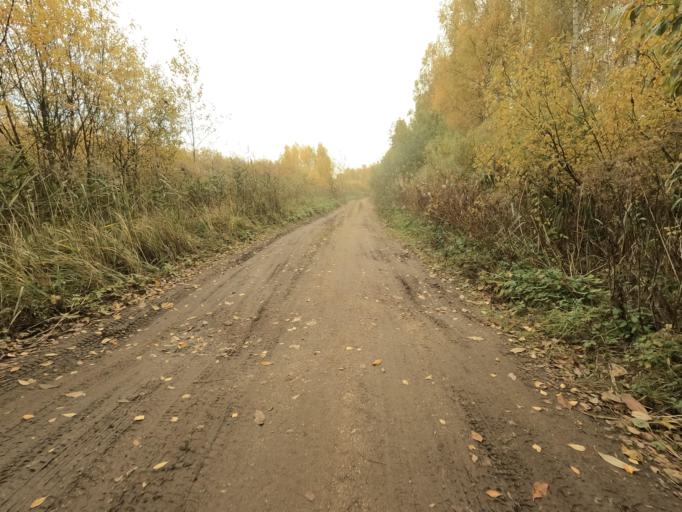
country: RU
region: Novgorod
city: Pankovka
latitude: 58.8728
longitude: 30.8898
